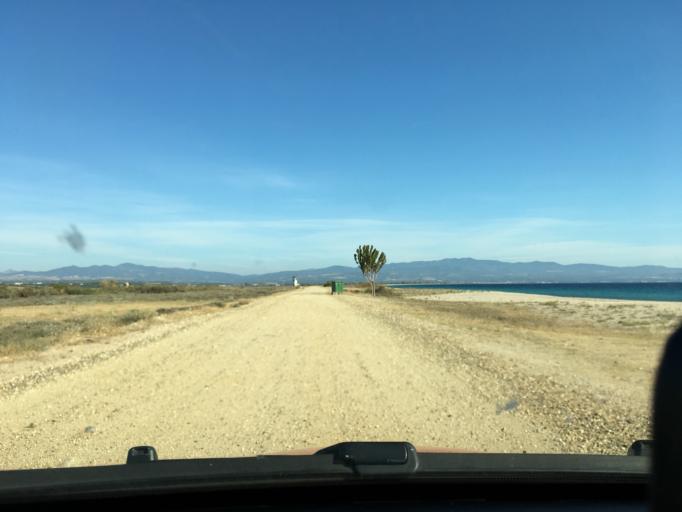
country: GR
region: Central Macedonia
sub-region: Nomos Chalkidikis
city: Nea Potidhaia
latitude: 40.2135
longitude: 23.3315
